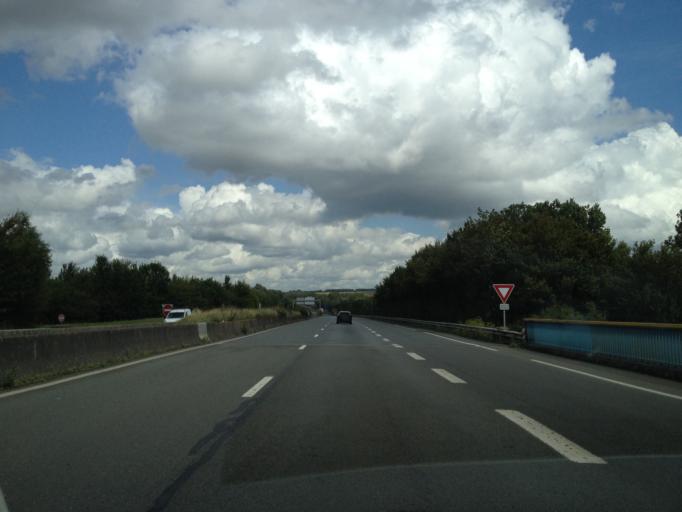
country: FR
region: Picardie
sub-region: Departement de la Somme
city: Abbeville
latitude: 50.1076
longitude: 1.7879
